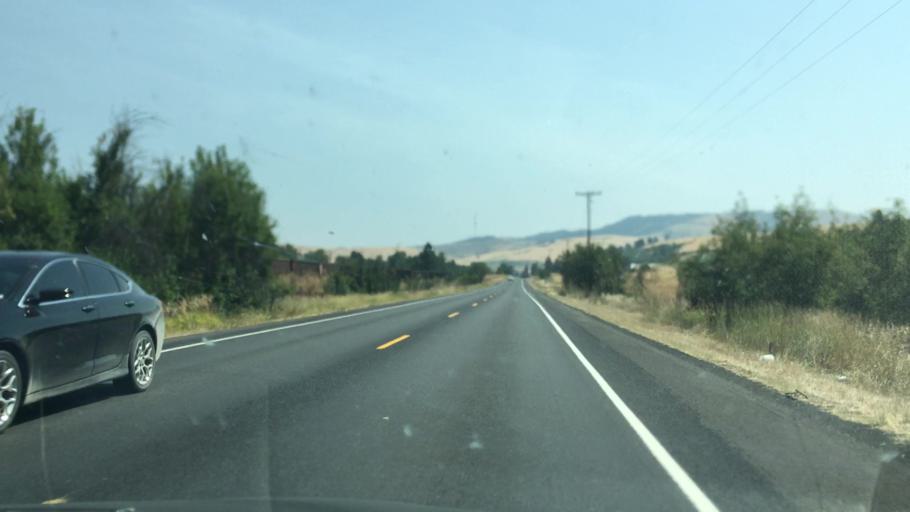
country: US
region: Idaho
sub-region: Nez Perce County
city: Lapwai
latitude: 46.3725
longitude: -116.6993
